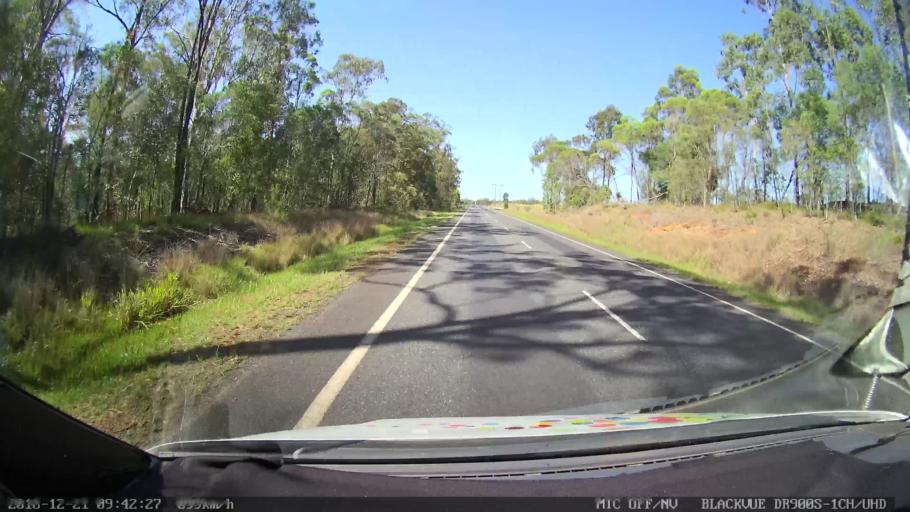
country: AU
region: New South Wales
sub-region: Clarence Valley
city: Grafton
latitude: -29.5965
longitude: 152.9466
